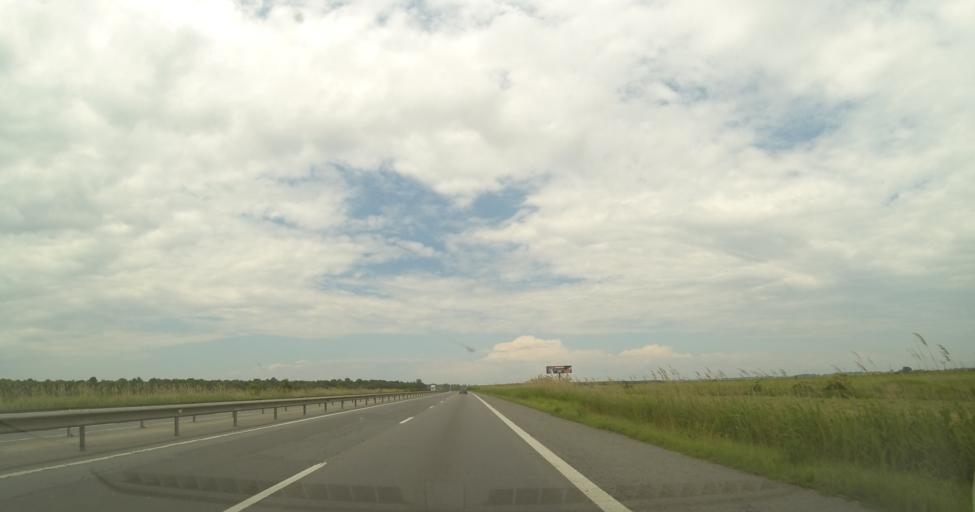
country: RO
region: Dambovita
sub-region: Comuna Corbii Mari
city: Grozavesti
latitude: 44.5944
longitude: 25.4609
